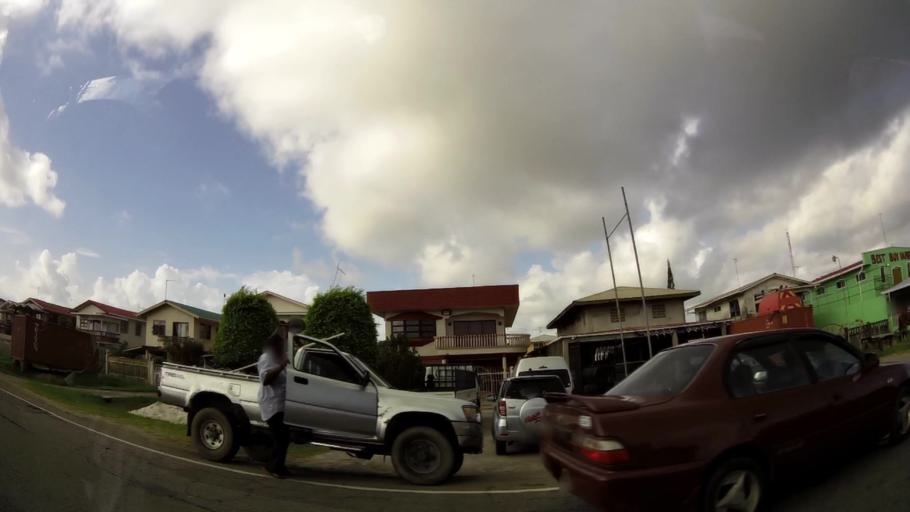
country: GY
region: Demerara-Mahaica
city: Mahaica Village
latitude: 6.7814
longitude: -58.0089
